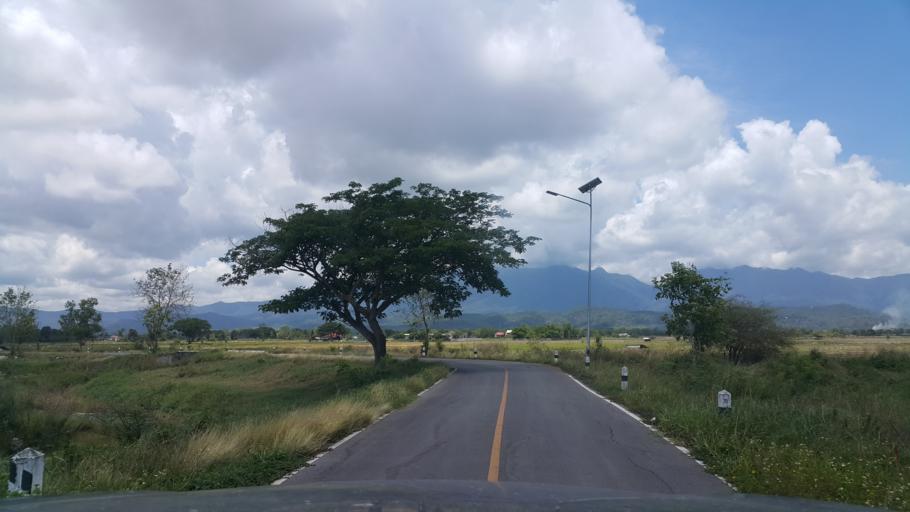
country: TH
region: Phayao
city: Phayao
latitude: 19.1849
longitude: 99.8554
